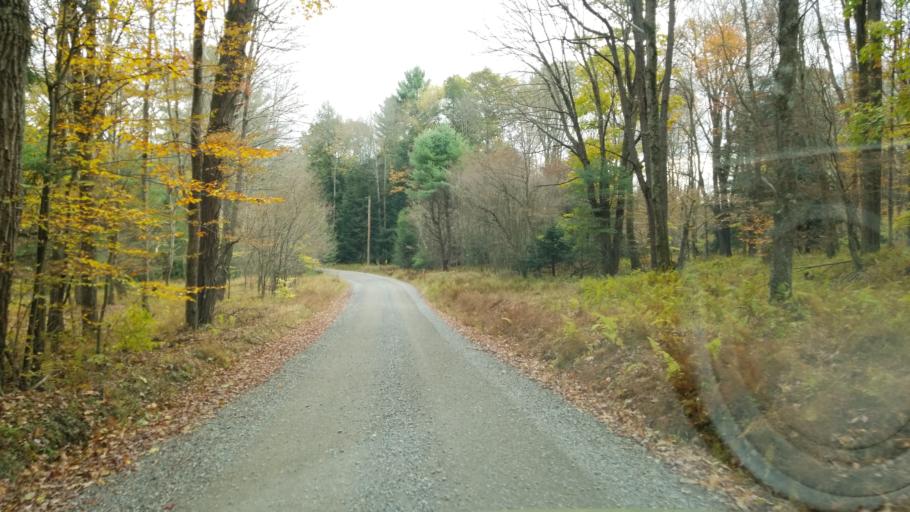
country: US
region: Pennsylvania
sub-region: Clearfield County
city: Clearfield
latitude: 41.1966
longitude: -78.4088
